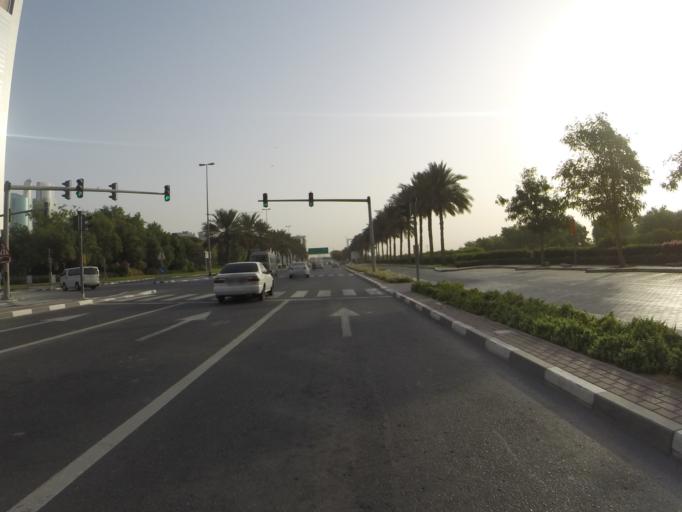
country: AE
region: Ash Shariqah
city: Sharjah
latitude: 25.2143
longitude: 55.2845
